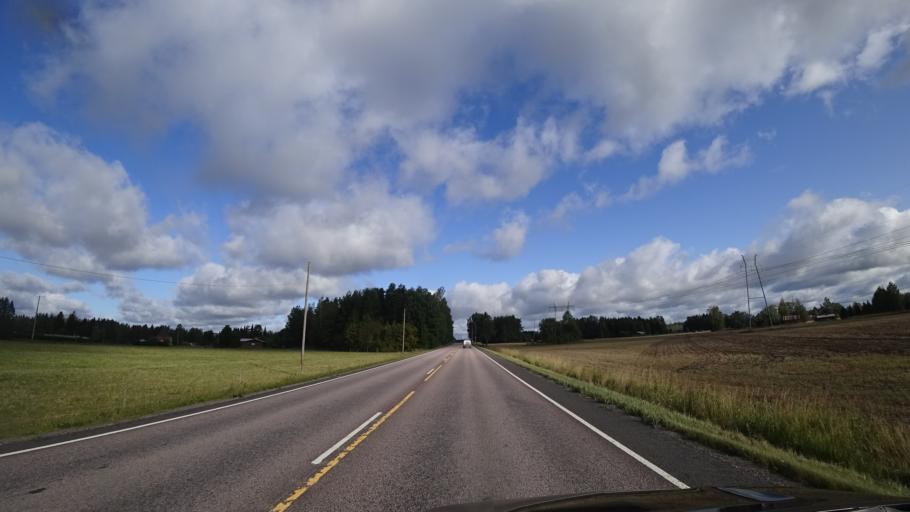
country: FI
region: Uusimaa
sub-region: Helsinki
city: Hyvinge
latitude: 60.5221
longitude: 24.9253
